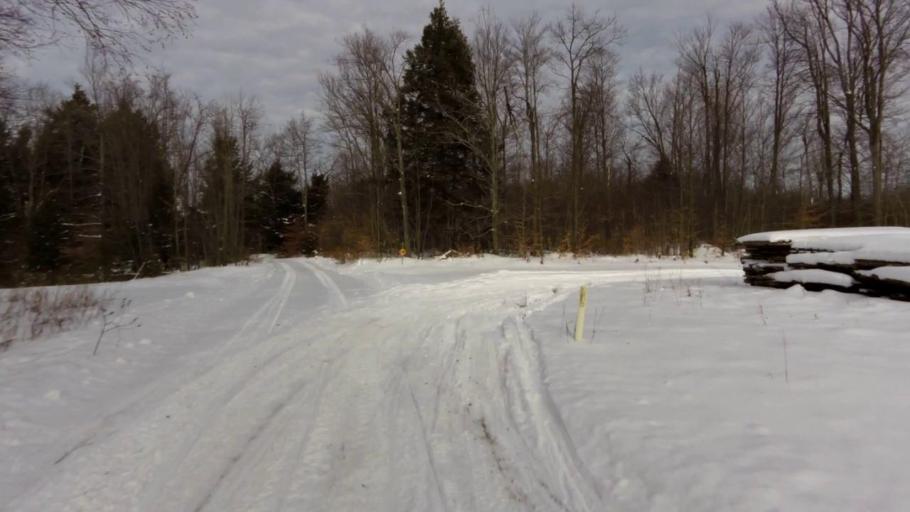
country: US
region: Pennsylvania
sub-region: McKean County
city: Foster Brook
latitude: 42.0170
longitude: -78.5501
